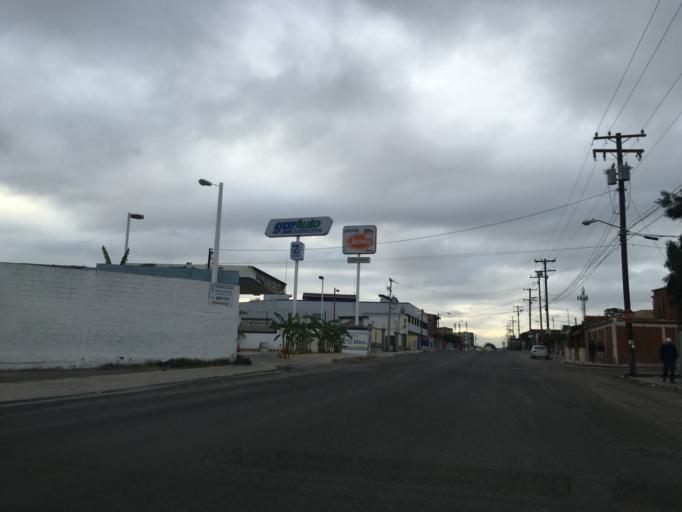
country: MX
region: Baja California
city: Tijuana
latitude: 32.5375
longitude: -117.0554
